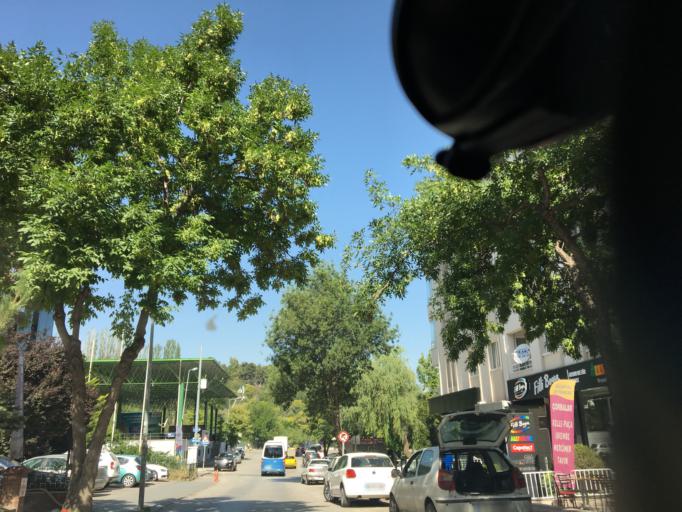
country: TR
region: Ankara
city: Ankara
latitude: 39.9029
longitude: 32.8469
